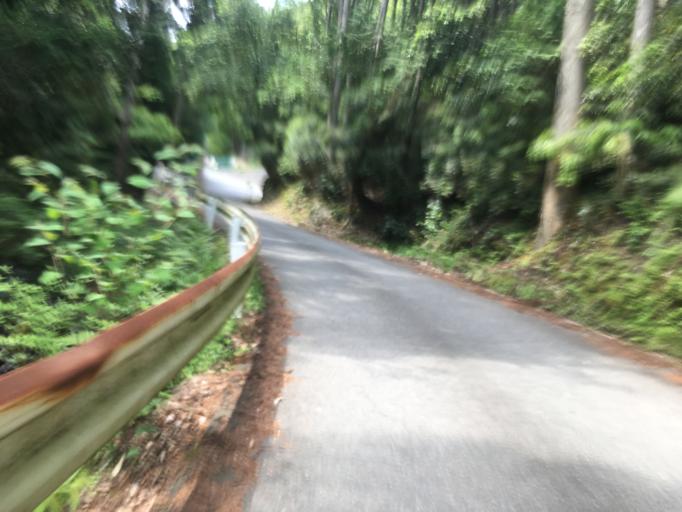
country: JP
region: Kyoto
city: Kameoka
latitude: 35.0329
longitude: 135.6332
